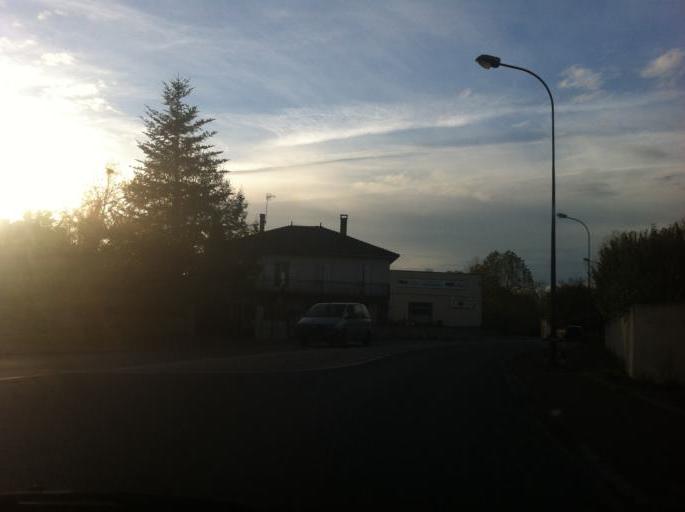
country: FR
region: Aquitaine
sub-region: Departement de la Dordogne
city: Mensignac
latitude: 45.2290
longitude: 0.5489
